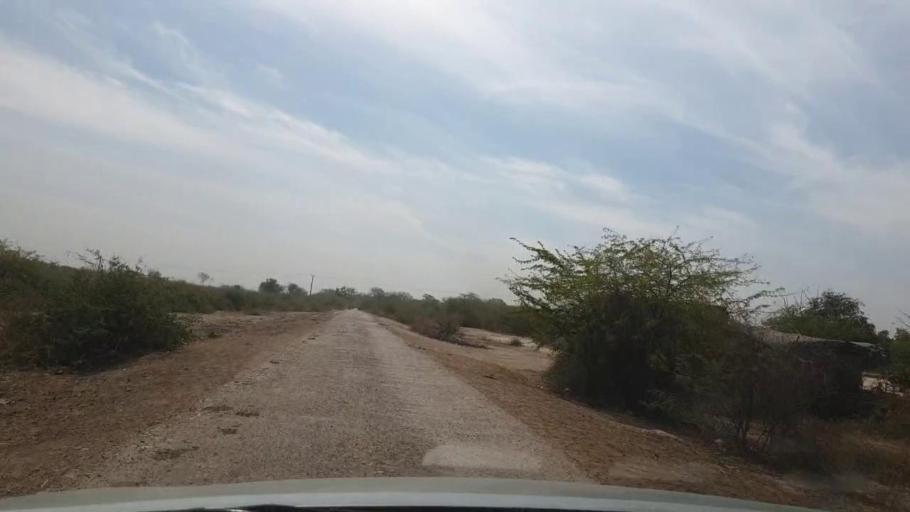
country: PK
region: Sindh
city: Nabisar
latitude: 25.0834
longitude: 69.5988
